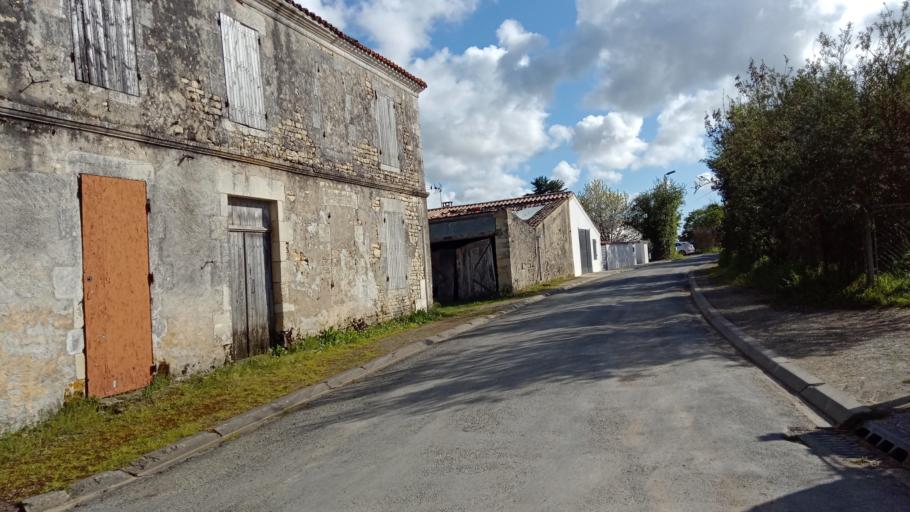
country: FR
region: Poitou-Charentes
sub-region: Departement de la Charente-Maritime
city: Verines
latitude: 46.1652
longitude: -0.9478
